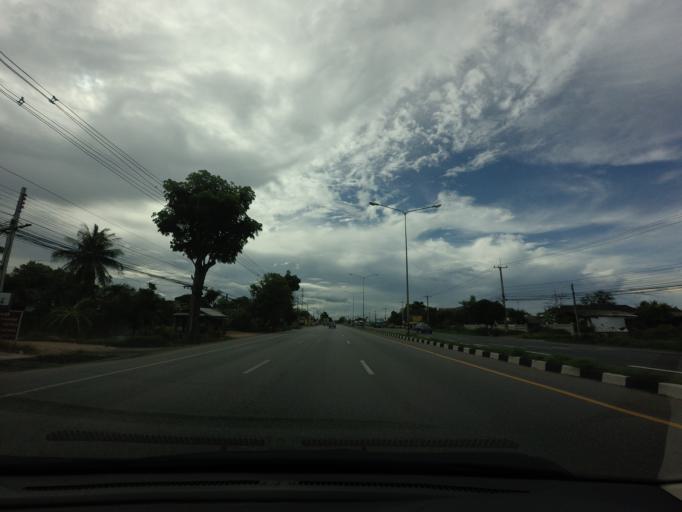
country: TH
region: Phetchaburi
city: Cha-am
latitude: 12.8664
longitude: 99.9190
